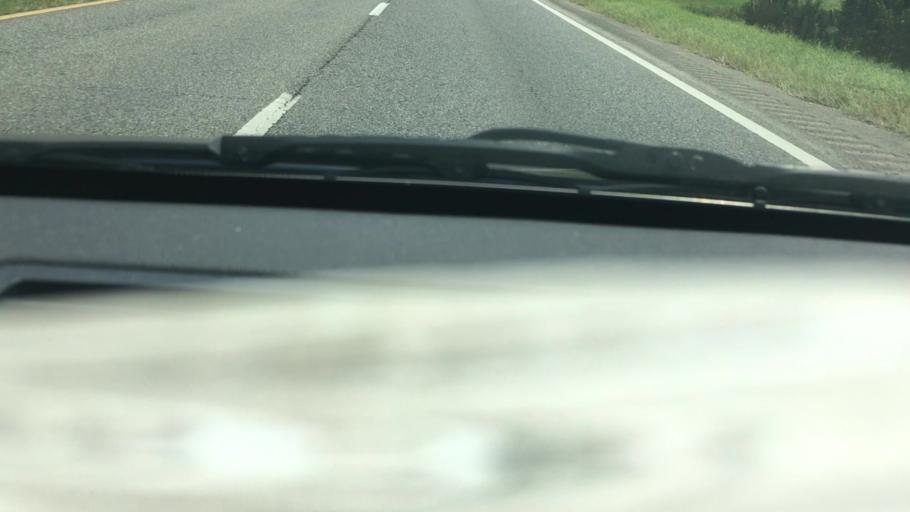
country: US
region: Alabama
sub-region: Pickens County
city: Gordo
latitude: 33.2703
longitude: -87.7415
